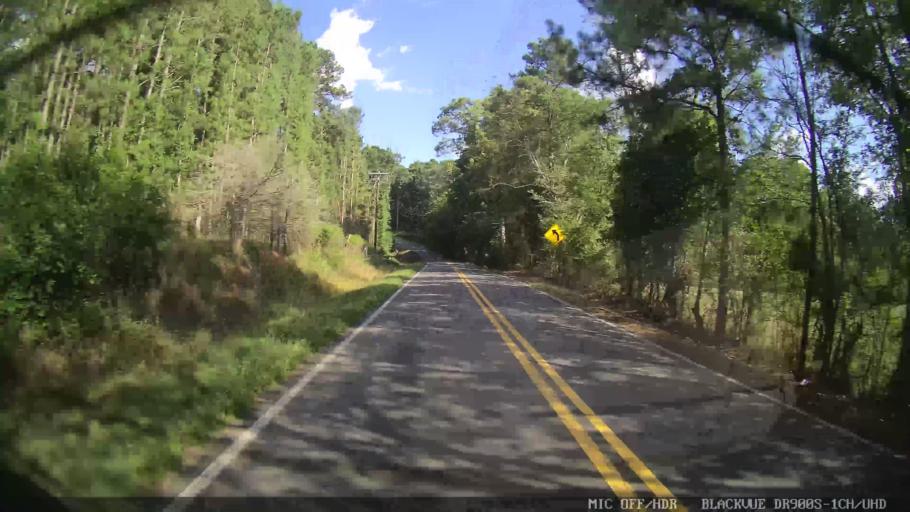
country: US
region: Georgia
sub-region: Floyd County
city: Lindale
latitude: 34.2043
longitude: -85.1175
